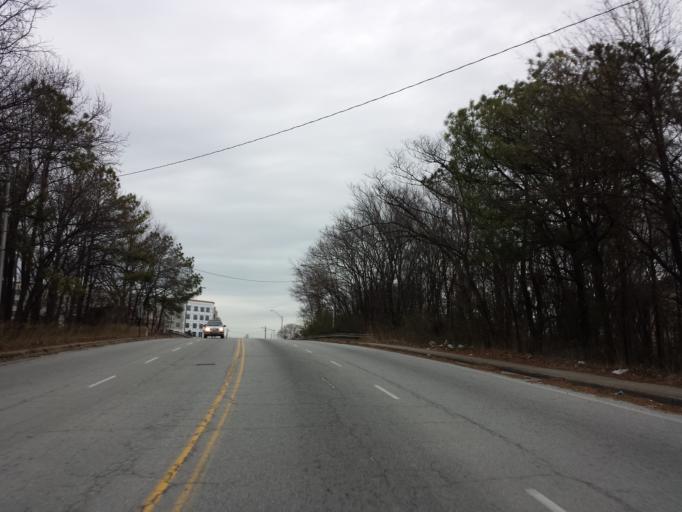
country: US
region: Georgia
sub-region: Fulton County
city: Atlanta
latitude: 33.7801
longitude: -84.4146
